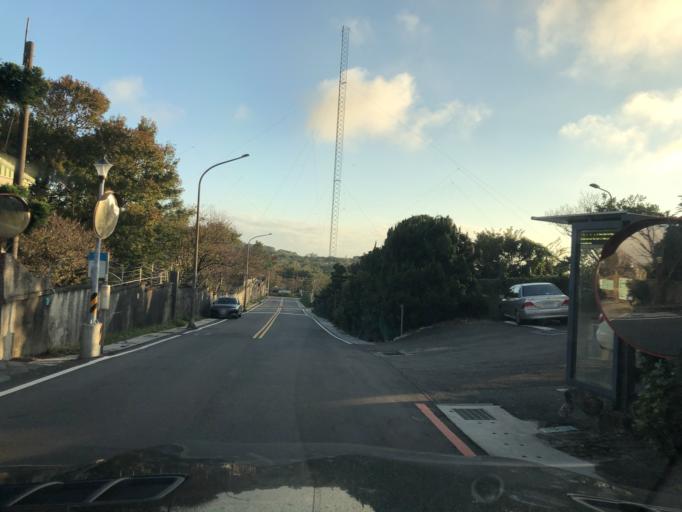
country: TW
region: Taipei
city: Taipei
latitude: 25.1452
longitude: 121.5577
